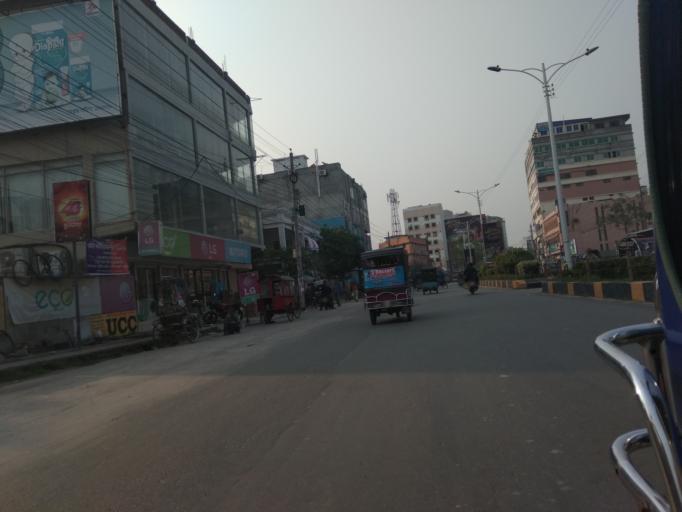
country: BD
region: Khulna
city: Khulna
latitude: 22.8145
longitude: 89.5551
